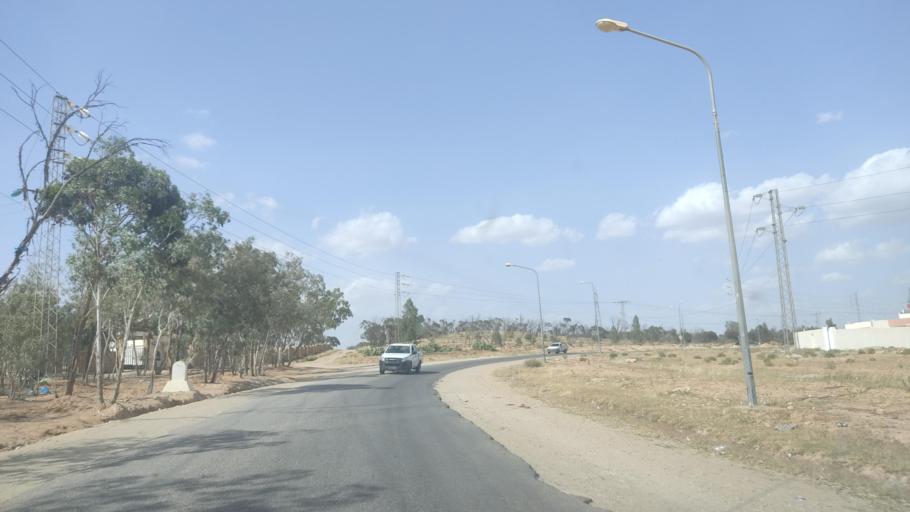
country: TN
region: Sidi Bu Zayd
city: Sidi Bouzid
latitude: 35.1084
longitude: 9.5390
